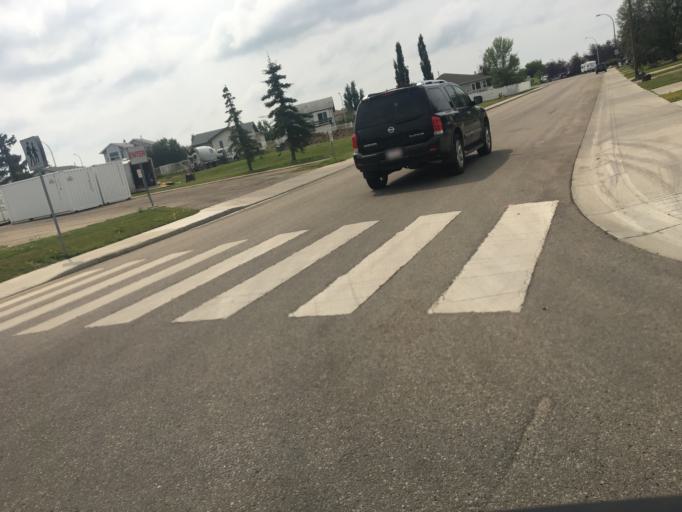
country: CA
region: Alberta
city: Grande Prairie
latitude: 55.1517
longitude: -118.8124
